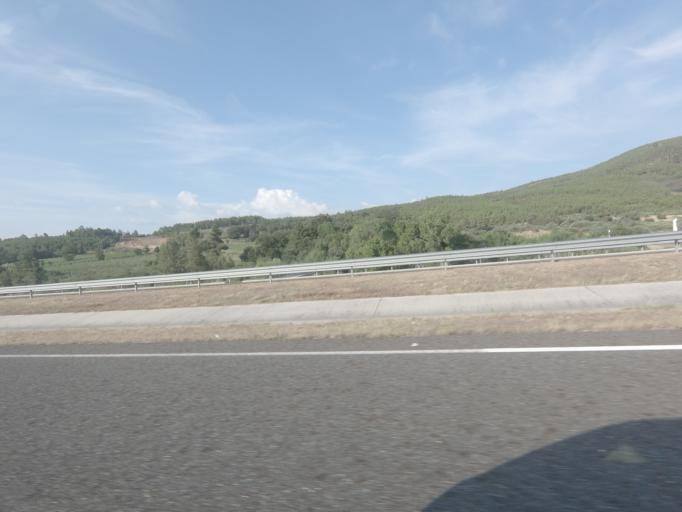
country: ES
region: Galicia
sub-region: Provincia de Ourense
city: Oimbra
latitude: 41.8678
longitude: -7.4322
